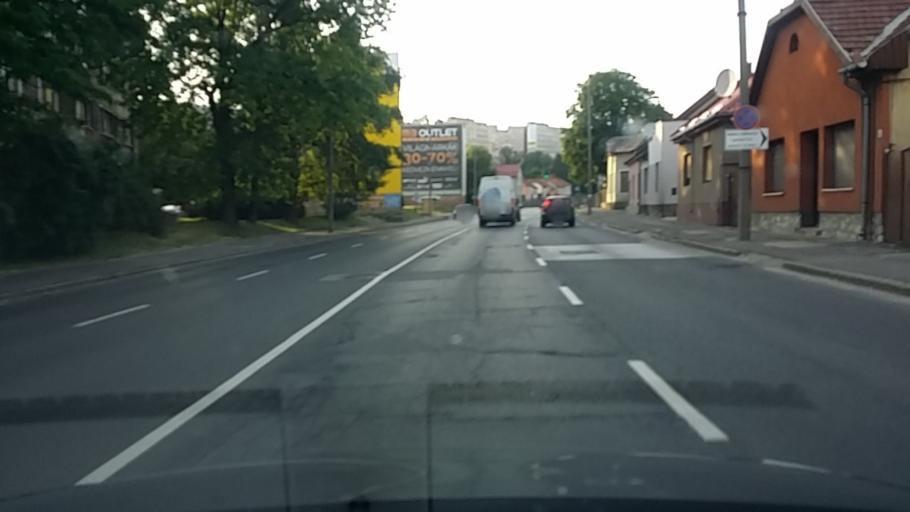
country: HU
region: Borsod-Abauj-Zemplen
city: Miskolc
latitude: 48.0749
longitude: 20.7864
